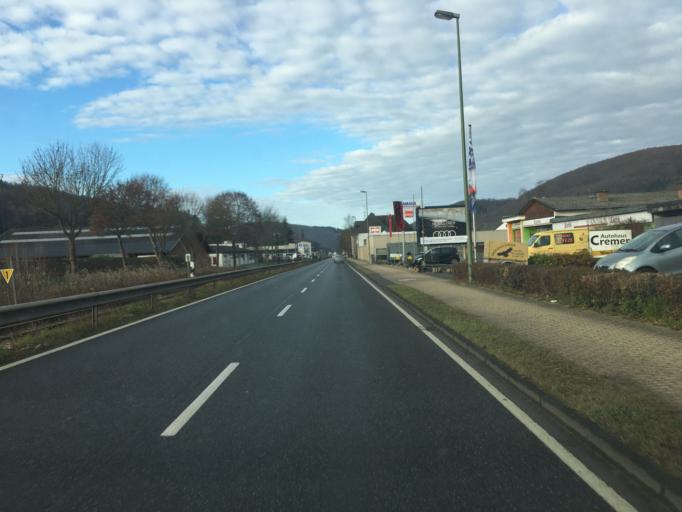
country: DE
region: North Rhine-Westphalia
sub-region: Regierungsbezirk Koln
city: Kall
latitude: 50.5687
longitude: 6.5253
